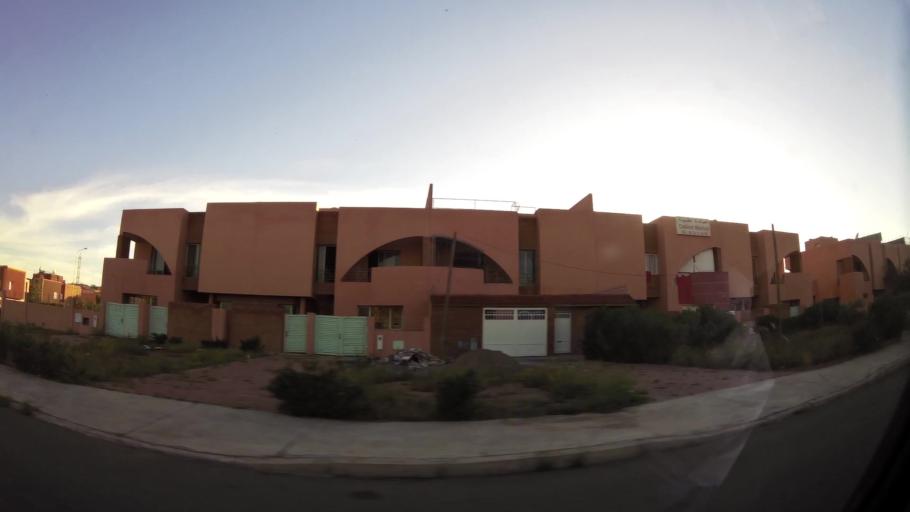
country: MA
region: Marrakech-Tensift-Al Haouz
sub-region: Marrakech
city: Marrakesh
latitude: 31.7460
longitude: -8.1061
